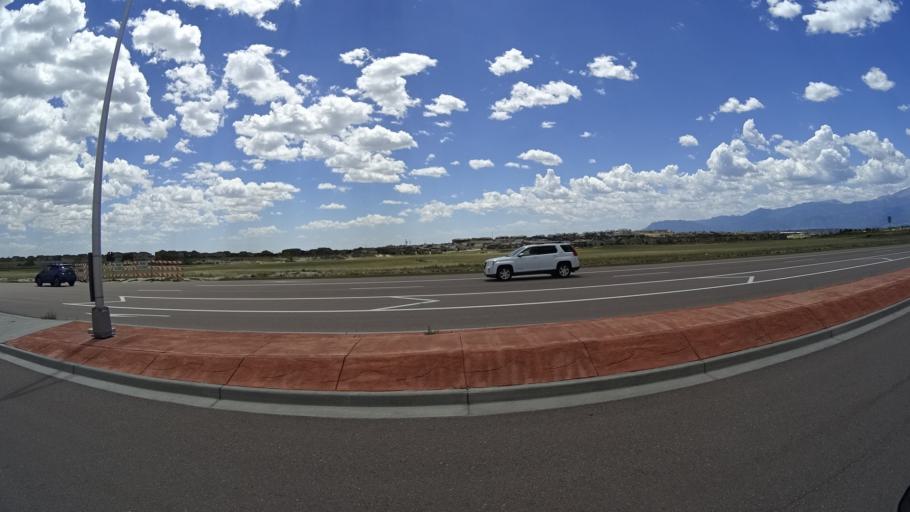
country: US
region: Colorado
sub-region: El Paso County
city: Black Forest
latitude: 38.9581
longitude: -104.7037
